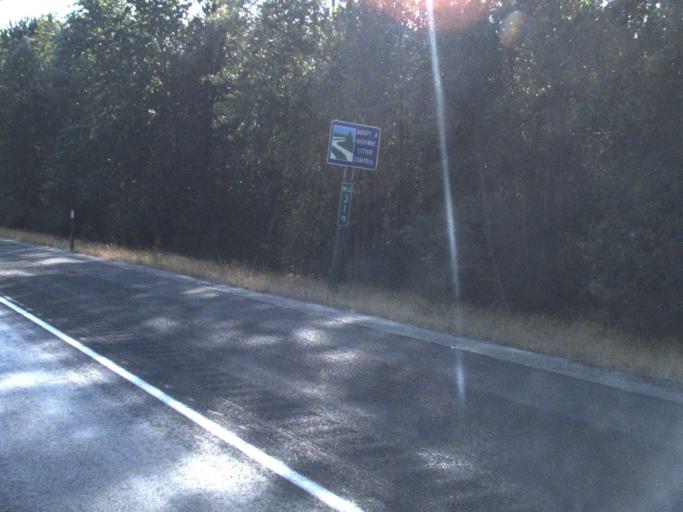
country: US
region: Washington
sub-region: Spokane County
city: Deer Park
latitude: 48.0923
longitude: -117.3249
